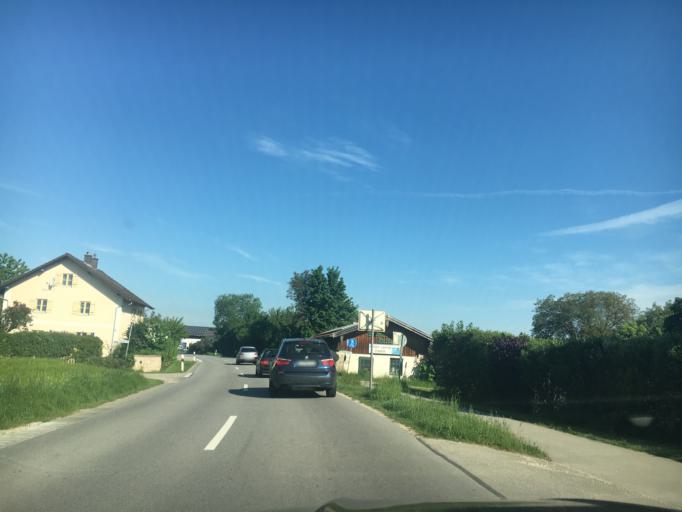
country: DE
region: Bavaria
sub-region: Upper Bavaria
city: Tacherting
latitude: 48.0900
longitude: 12.5912
